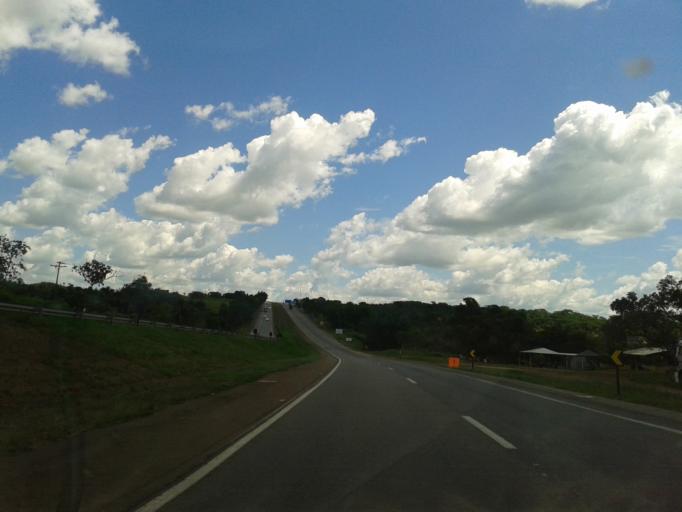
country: BR
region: Goias
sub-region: Hidrolandia
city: Hidrolandia
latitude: -17.1513
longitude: -49.2155
